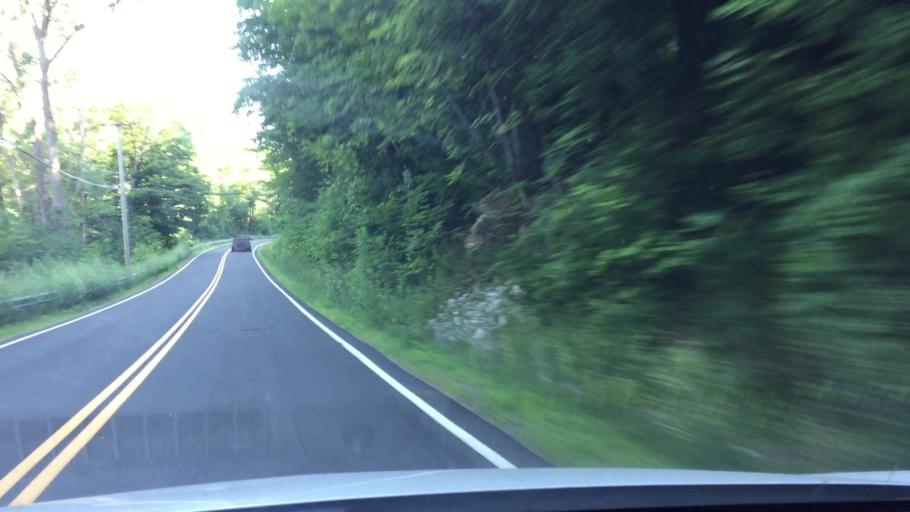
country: US
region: Massachusetts
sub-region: Berkshire County
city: Lee
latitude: 42.2789
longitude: -73.2394
